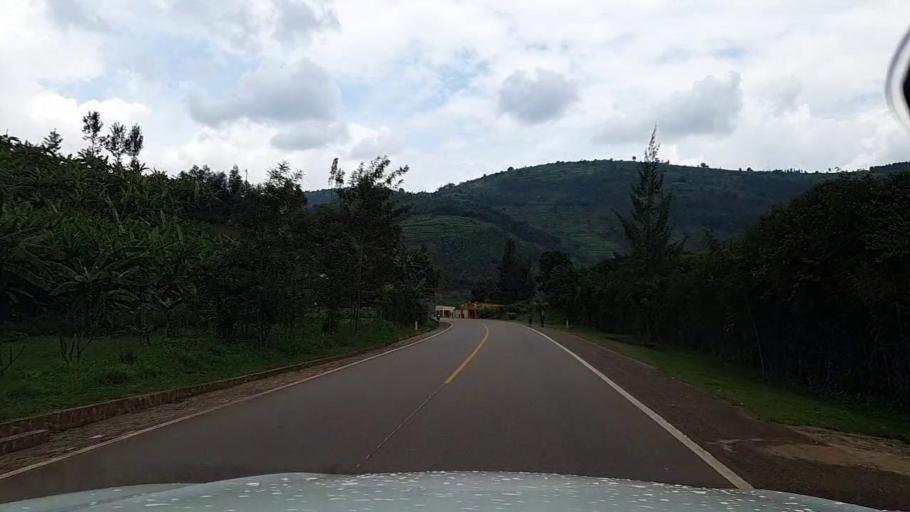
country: RW
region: Northern Province
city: Byumba
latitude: -1.7141
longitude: 30.1234
